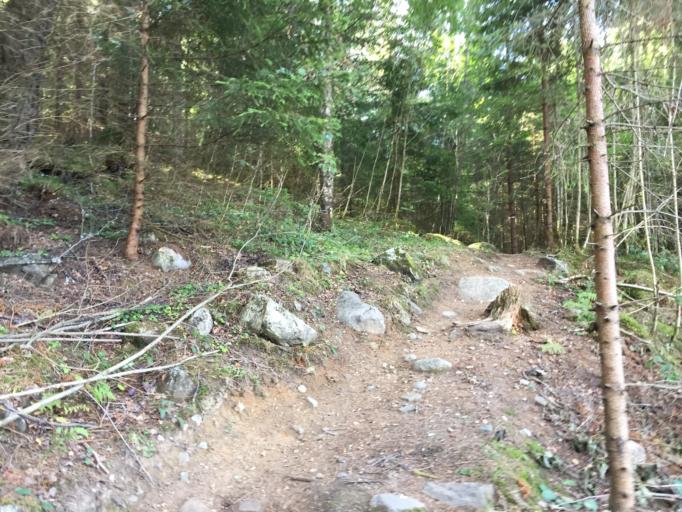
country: NO
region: Akershus
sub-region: Skedsmo
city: Lillestrom
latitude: 59.9250
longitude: 11.0195
